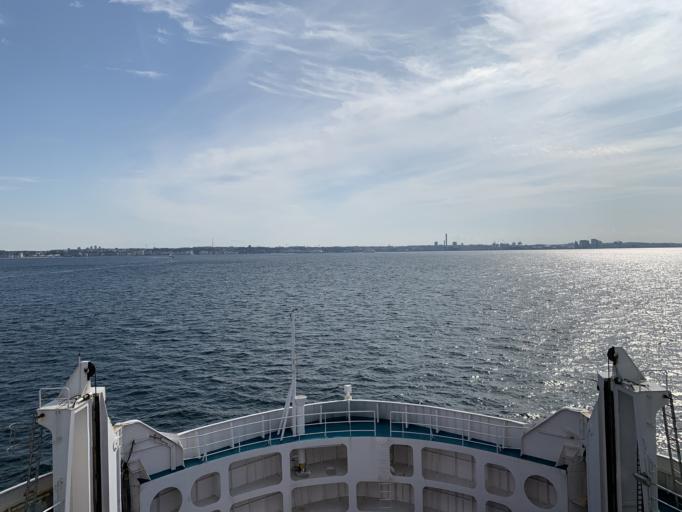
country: DK
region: Capital Region
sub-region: Helsingor Kommune
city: Helsingor
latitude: 56.0348
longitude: 12.6332
